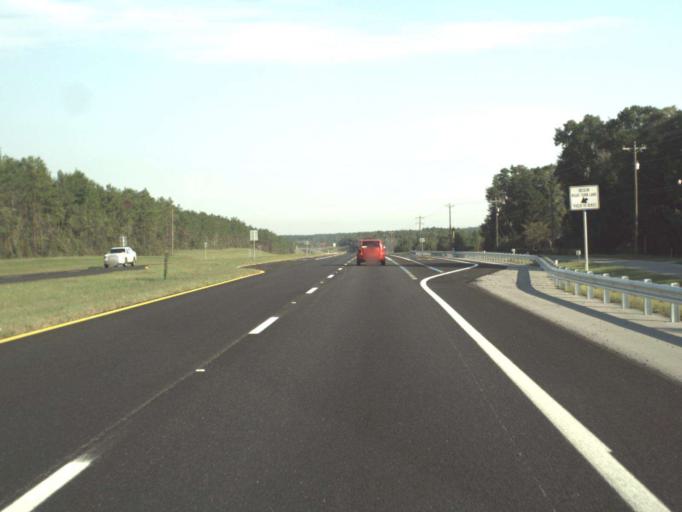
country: US
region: Florida
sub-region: Bay County
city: Laguna Beach
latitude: 30.5031
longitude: -85.8410
